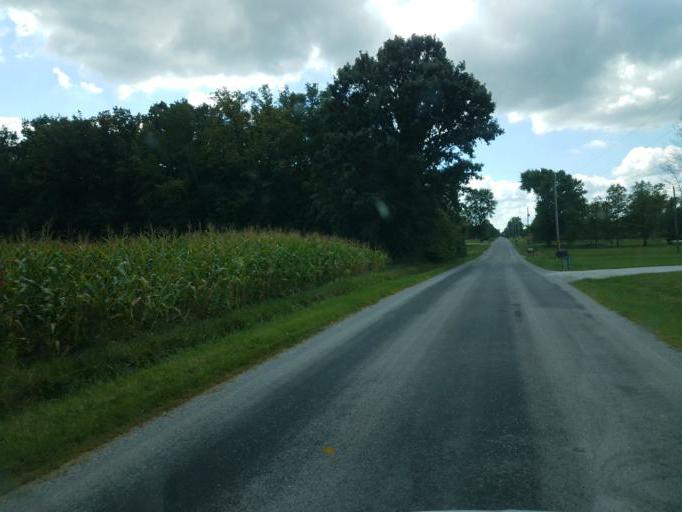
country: US
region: Ohio
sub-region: Medina County
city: Lodi
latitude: 41.0931
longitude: -82.0947
